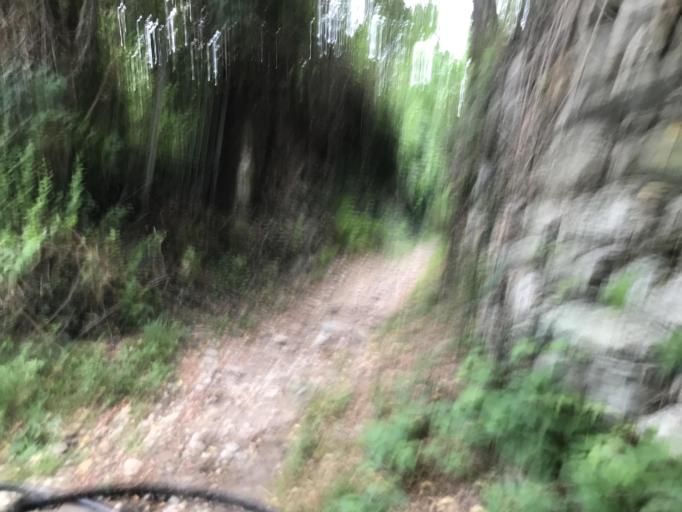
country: IT
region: Lombardy
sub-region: Provincia di Varese
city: Casalzuigno
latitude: 45.8996
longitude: 8.6972
